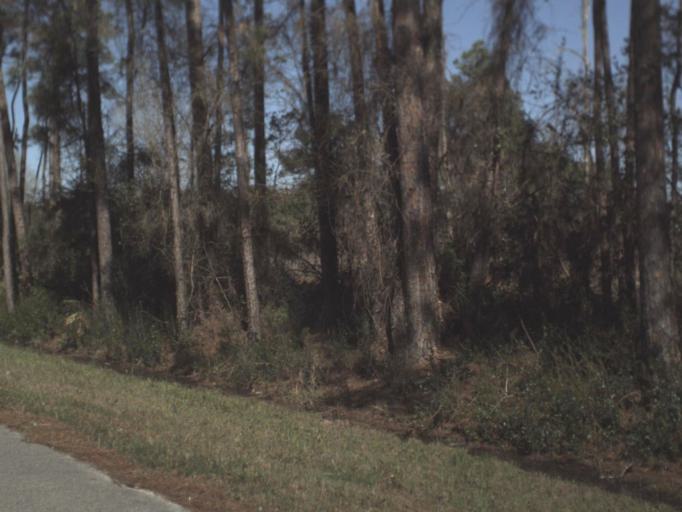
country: US
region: Florida
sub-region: Gulf County
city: Wewahitchka
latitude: 29.9545
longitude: -85.1794
